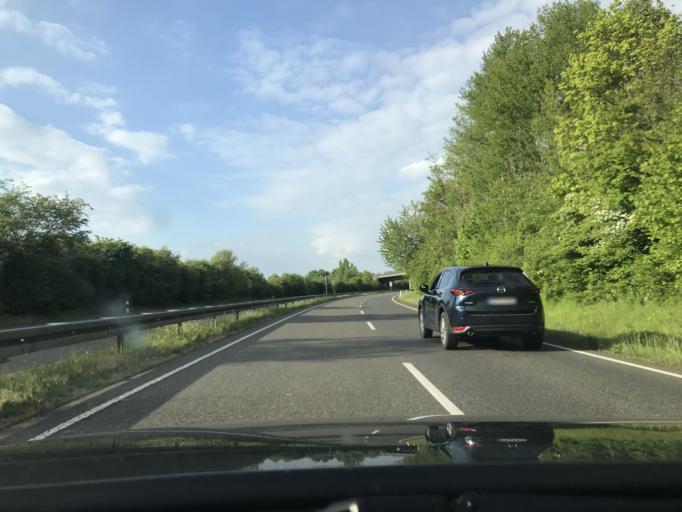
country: DE
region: North Rhine-Westphalia
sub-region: Regierungsbezirk Koln
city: Erftstadt
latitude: 50.8160
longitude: 6.8070
